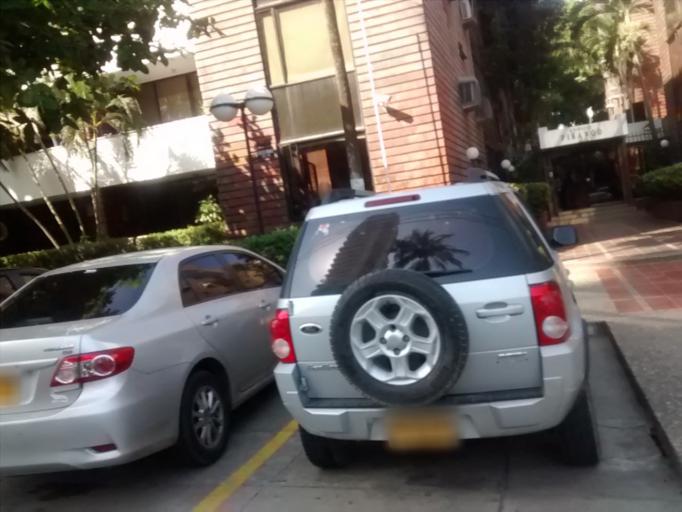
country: CO
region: Bolivar
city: Cartagena
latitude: 10.3921
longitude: -75.5475
